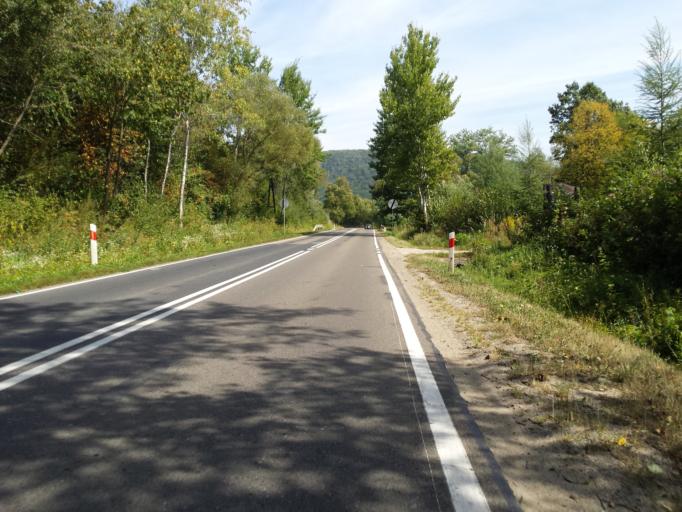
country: PL
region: Subcarpathian Voivodeship
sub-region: Powiat leski
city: Lesko
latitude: 49.4333
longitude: 22.3397
